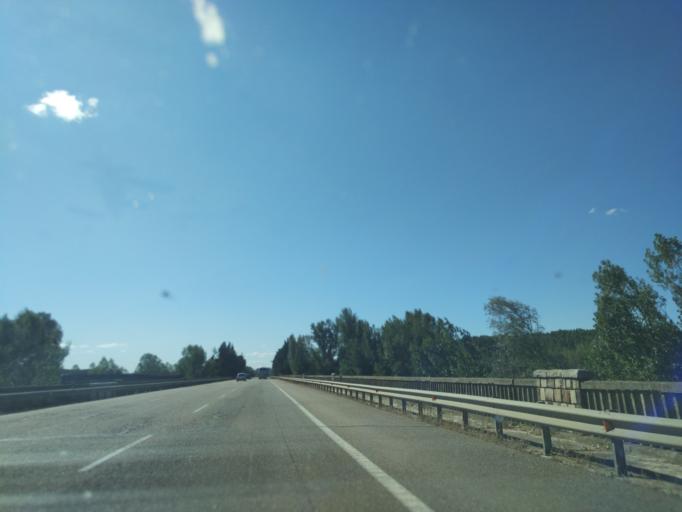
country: ES
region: Castille and Leon
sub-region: Provincia de Zamora
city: Castrogonzalo
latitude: 41.9837
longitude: -5.6239
